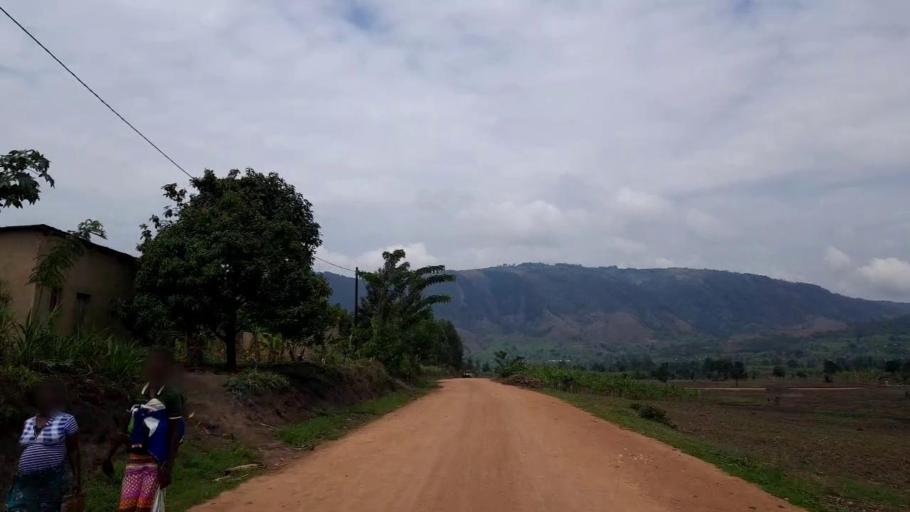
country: RW
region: Northern Province
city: Byumba
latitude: -1.5000
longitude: 30.2098
